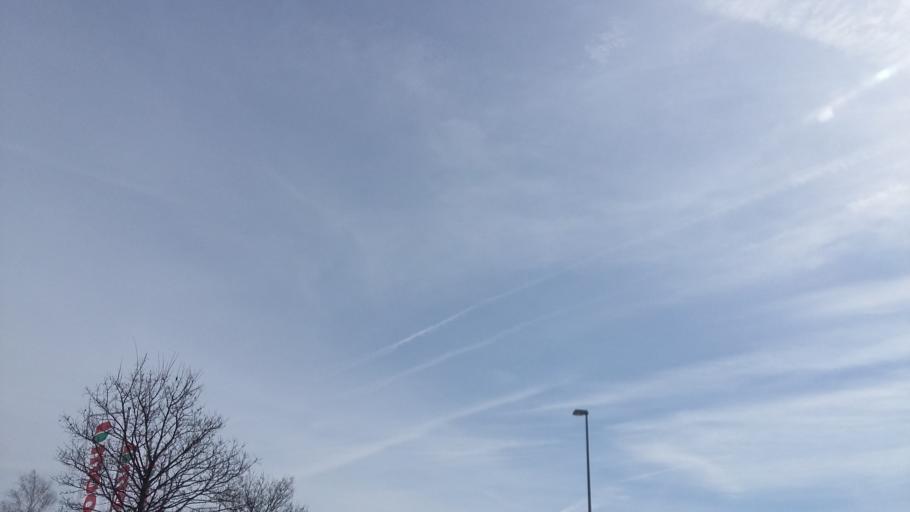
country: DE
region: Baden-Wuerttemberg
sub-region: Tuebingen Region
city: Leutkirch im Allgau
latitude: 47.8298
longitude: 10.0053
